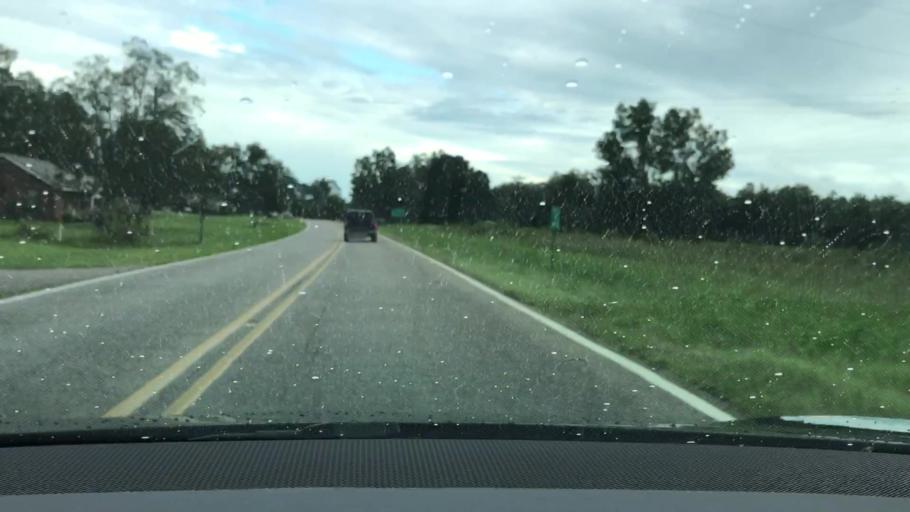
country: US
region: Alabama
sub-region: Geneva County
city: Samson
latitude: 31.1182
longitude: -86.1221
